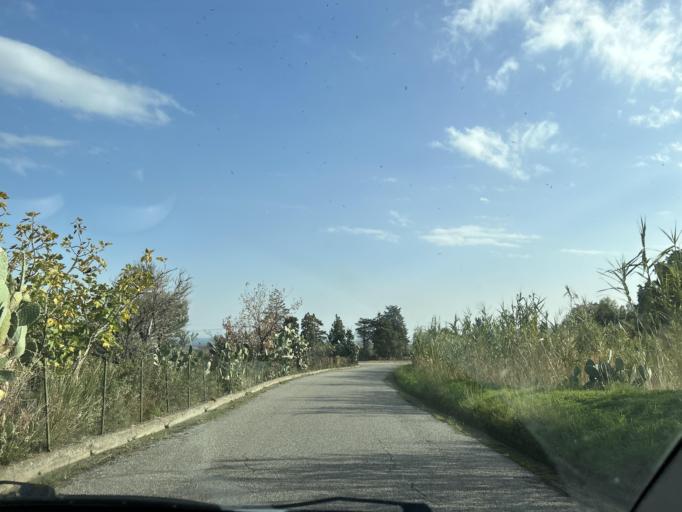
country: IT
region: Calabria
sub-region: Provincia di Catanzaro
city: Montepaone Lido
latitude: 38.7152
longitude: 16.5227
